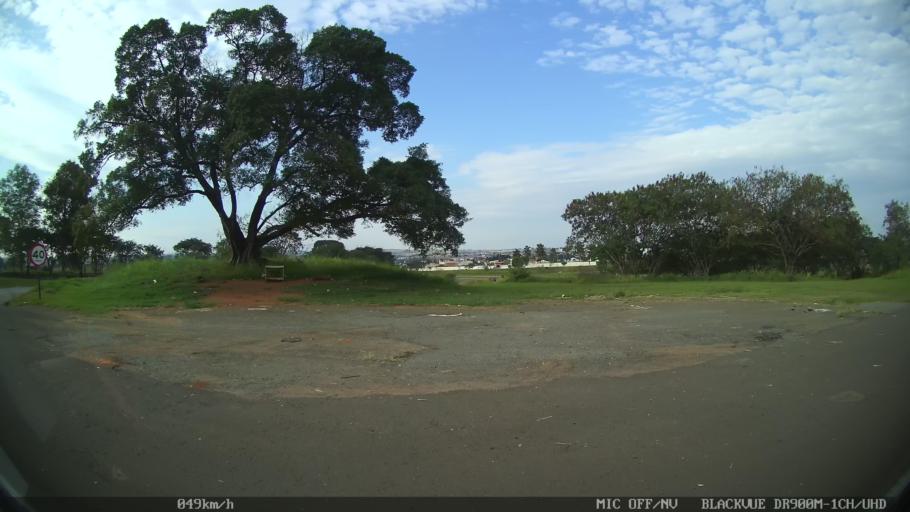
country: BR
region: Sao Paulo
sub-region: Cosmopolis
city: Cosmopolis
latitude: -22.6330
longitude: -47.2070
